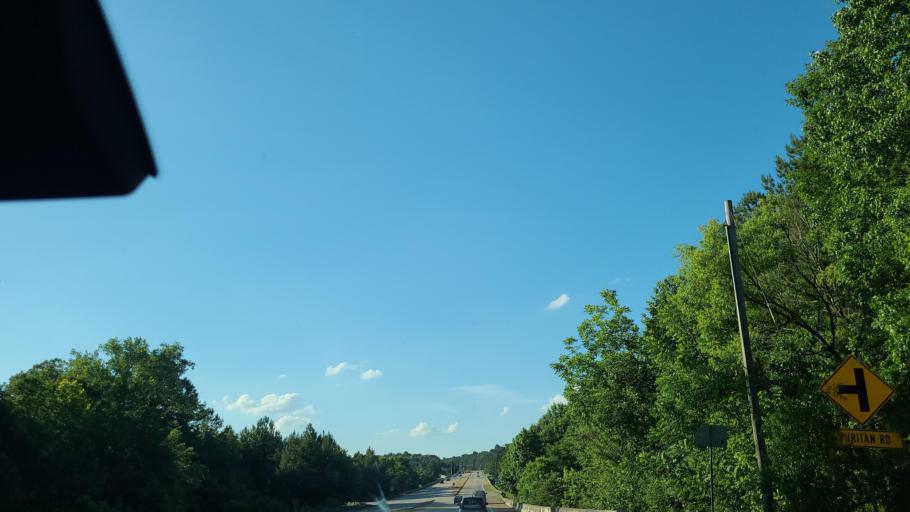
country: US
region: Georgia
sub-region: Oconee County
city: Watkinsville
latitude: 33.9102
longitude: -83.4044
